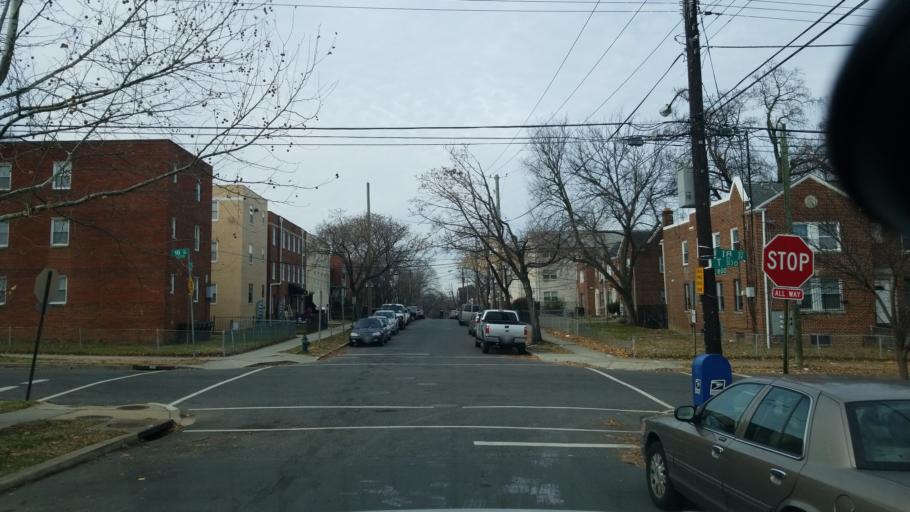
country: US
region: Maryland
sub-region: Prince George's County
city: Hillcrest Heights
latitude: 38.8673
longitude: -76.9788
